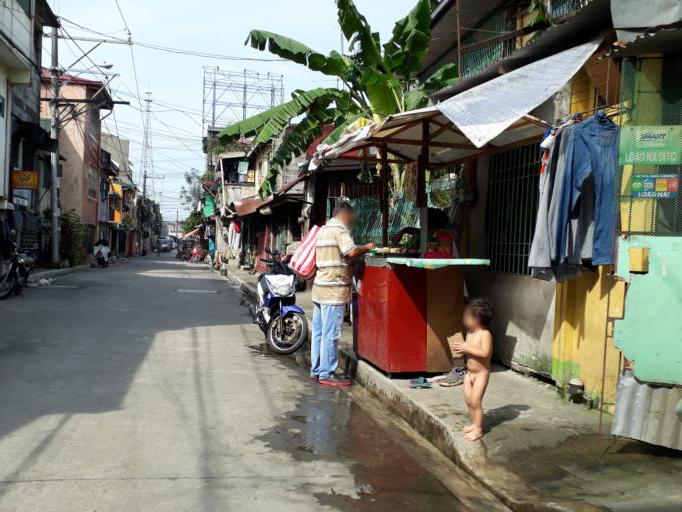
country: PH
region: Calabarzon
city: Del Monte
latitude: 14.6657
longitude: 121.0016
